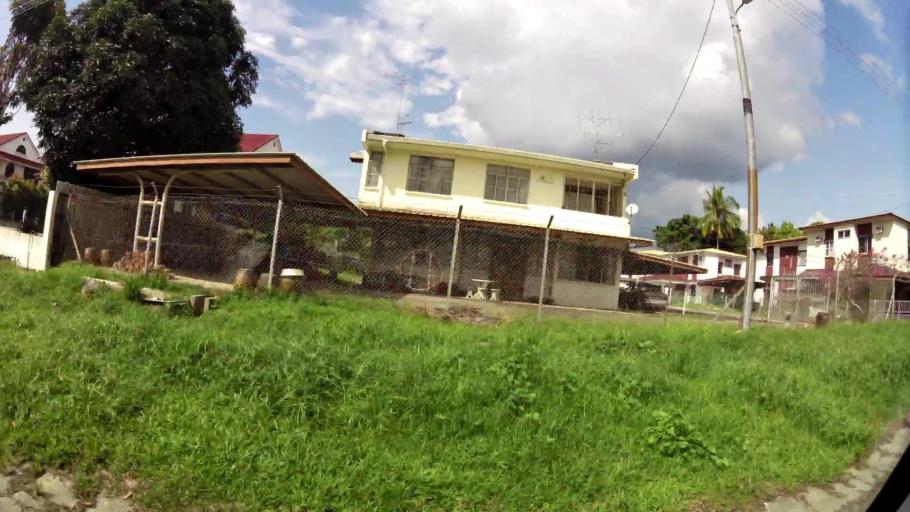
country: BN
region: Brunei and Muara
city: Bandar Seri Begawan
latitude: 4.9546
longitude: 114.9495
